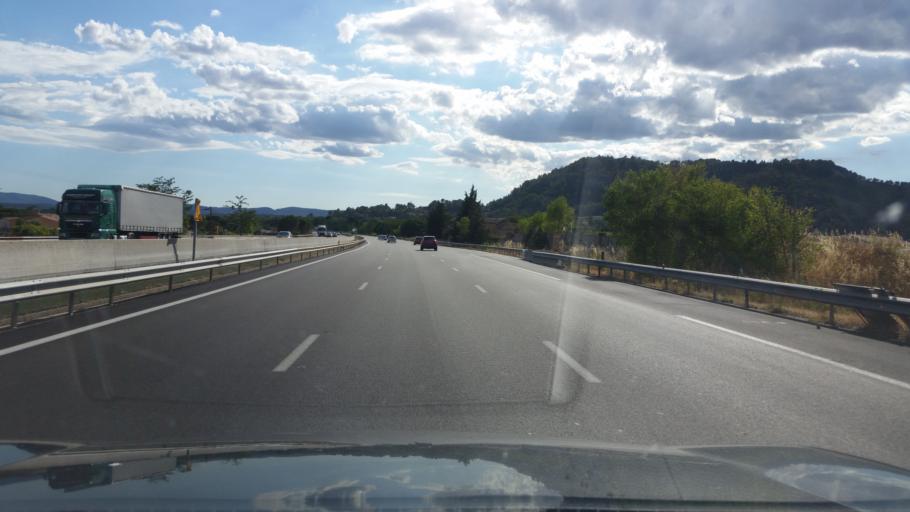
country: FR
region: Provence-Alpes-Cote d'Azur
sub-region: Departement du Var
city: Vidauban
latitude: 43.4137
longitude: 6.4289
